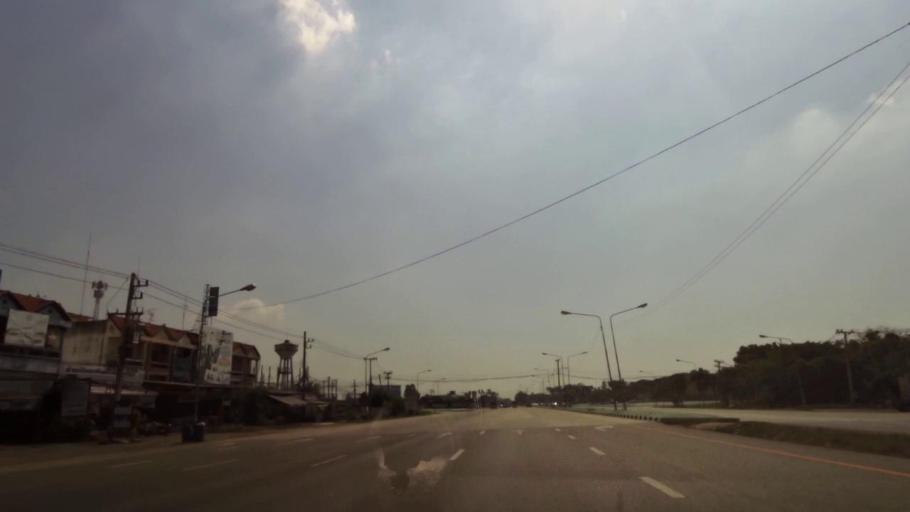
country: TH
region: Phichit
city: Bueng Na Rang
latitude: 16.1256
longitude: 100.1256
